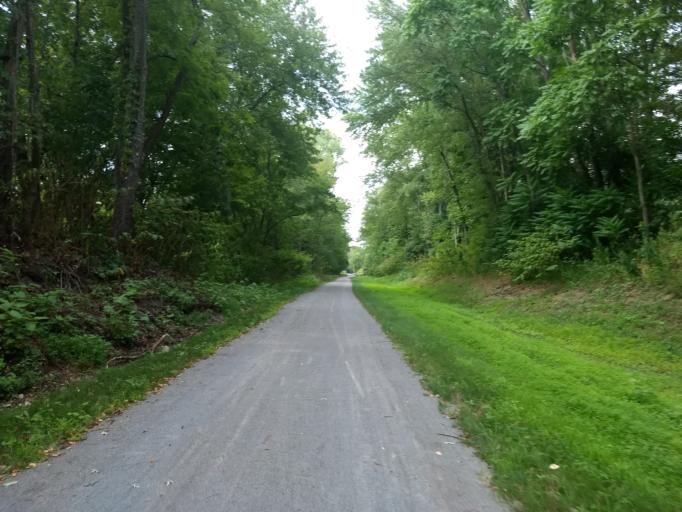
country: US
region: Pennsylvania
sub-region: Armstrong County
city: Freeport
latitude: 40.6543
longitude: -79.6881
